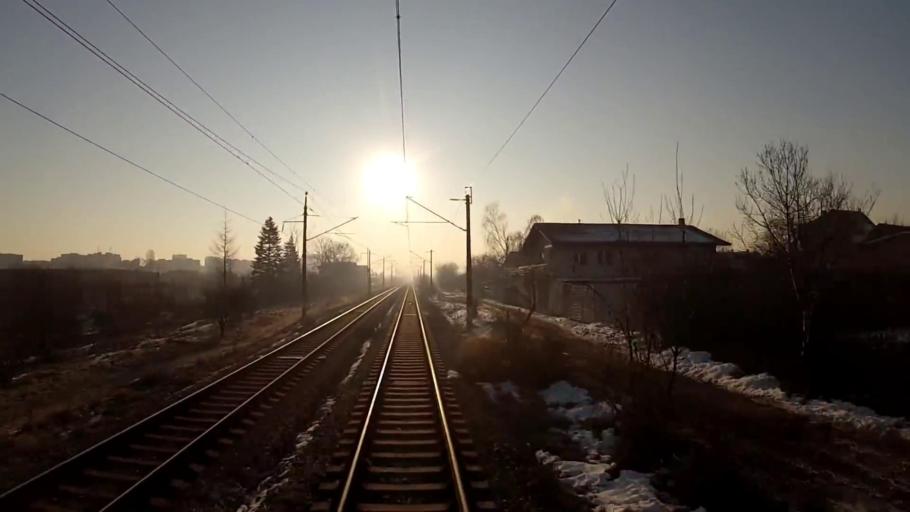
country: BG
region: Sofia-Capital
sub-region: Stolichna Obshtina
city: Sofia
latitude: 42.7343
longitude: 23.2686
